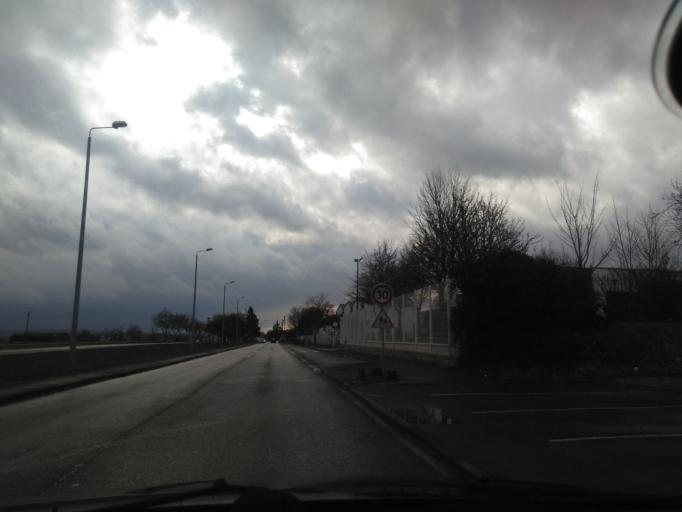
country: FR
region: Picardie
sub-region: Departement de l'Aisne
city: Laon
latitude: 49.5622
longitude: 3.6425
